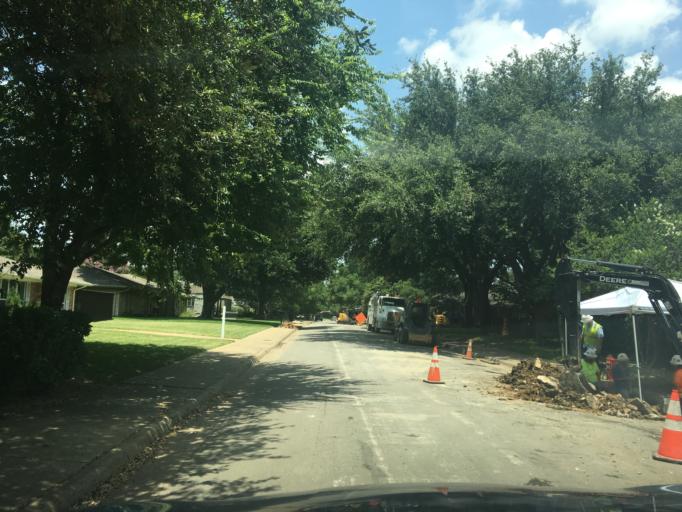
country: US
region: Texas
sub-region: Dallas County
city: Addison
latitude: 32.9133
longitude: -96.8433
